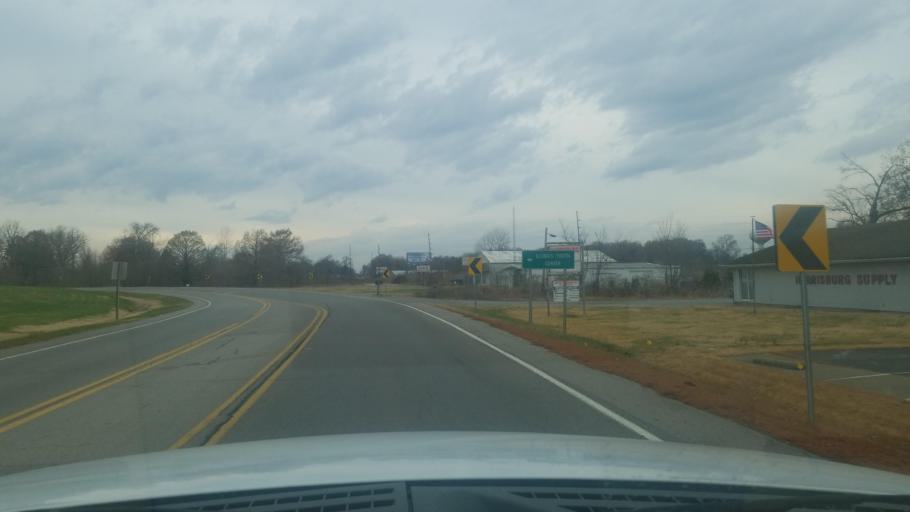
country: US
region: Illinois
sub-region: Saline County
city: Harrisburg
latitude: 37.7389
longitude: -88.5581
